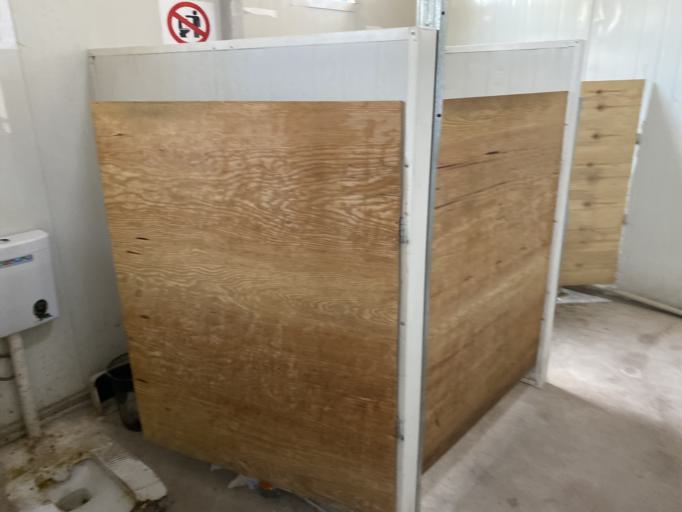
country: KZ
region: Qaraghandy
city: Balqash
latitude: 46.6451
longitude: 74.3940
